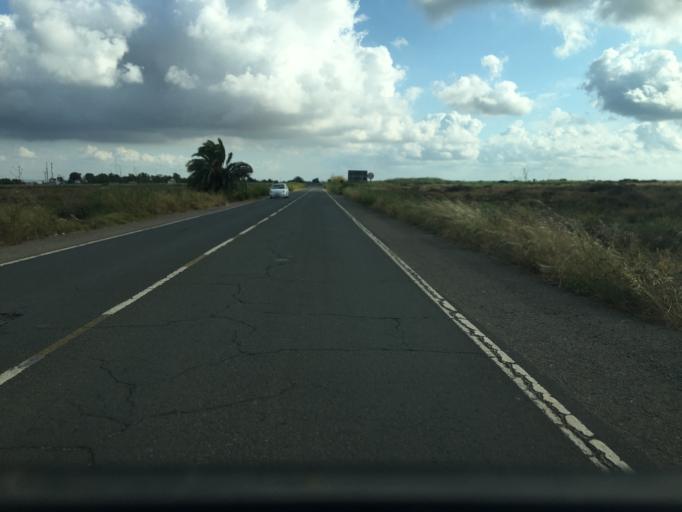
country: ES
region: Murcia
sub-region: Murcia
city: Los Alcazares
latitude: 37.7102
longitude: -0.8624
